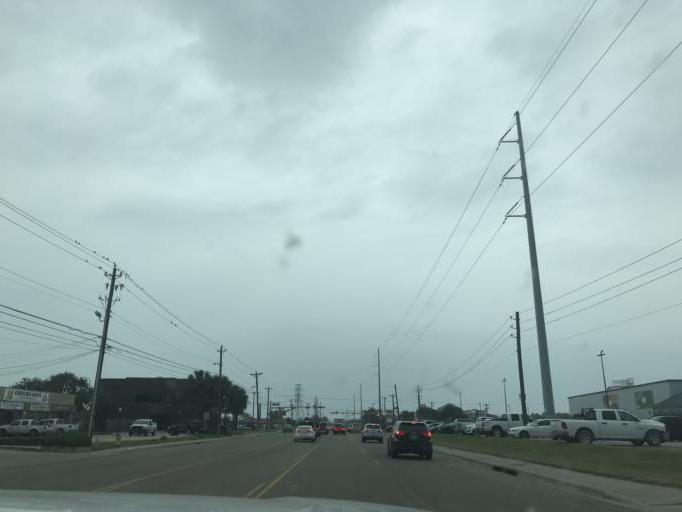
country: US
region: Texas
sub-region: Nueces County
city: Corpus Christi
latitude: 27.6929
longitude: -97.3651
